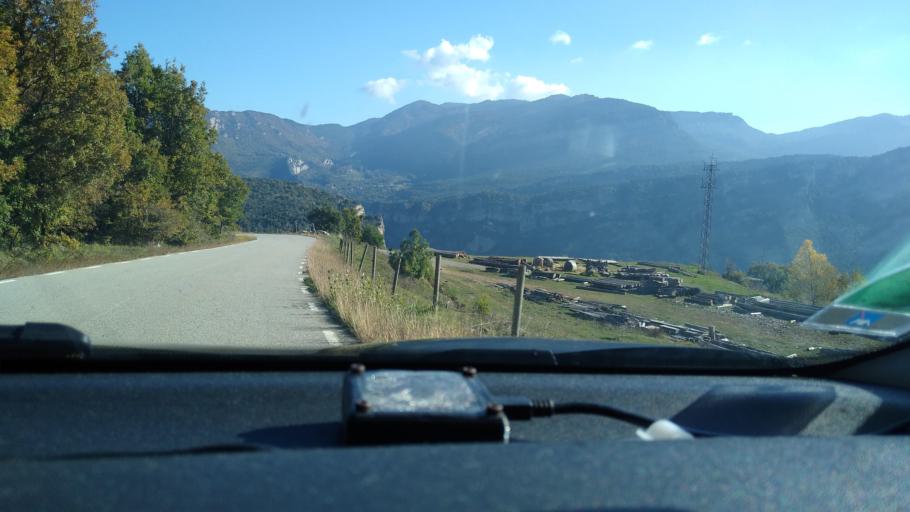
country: ES
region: Catalonia
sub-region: Provincia de Barcelona
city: Vallcebre
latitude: 42.1864
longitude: 1.8487
